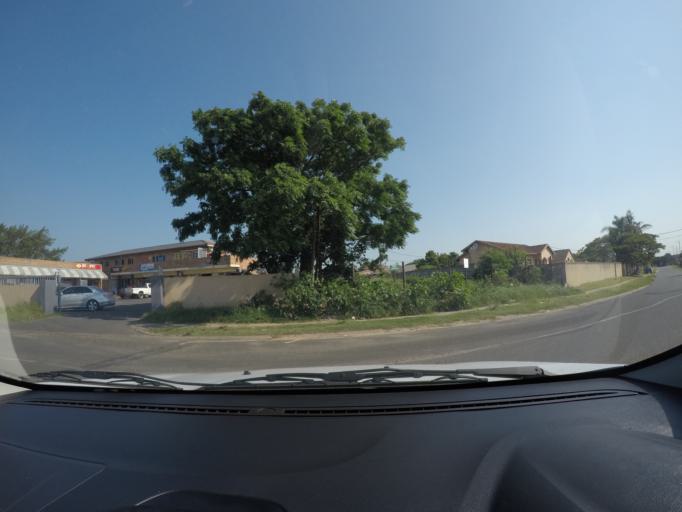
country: ZA
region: KwaZulu-Natal
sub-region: uThungulu District Municipality
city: Richards Bay
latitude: -28.7173
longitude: 32.0417
